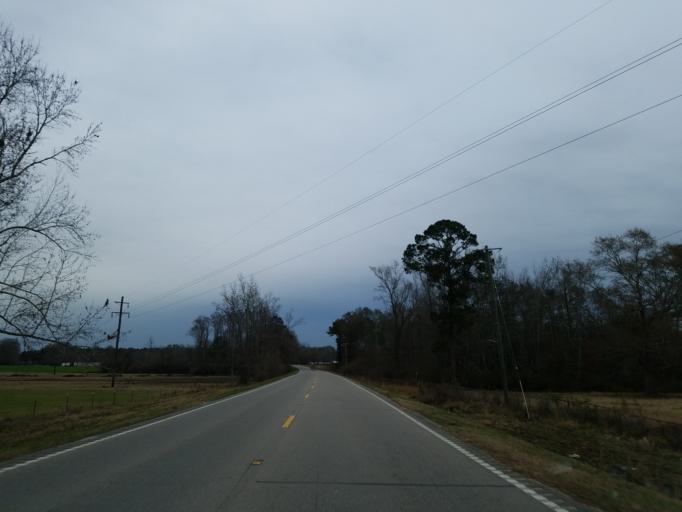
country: US
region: Mississippi
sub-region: Forrest County
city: Glendale
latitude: 31.4862
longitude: -89.2812
